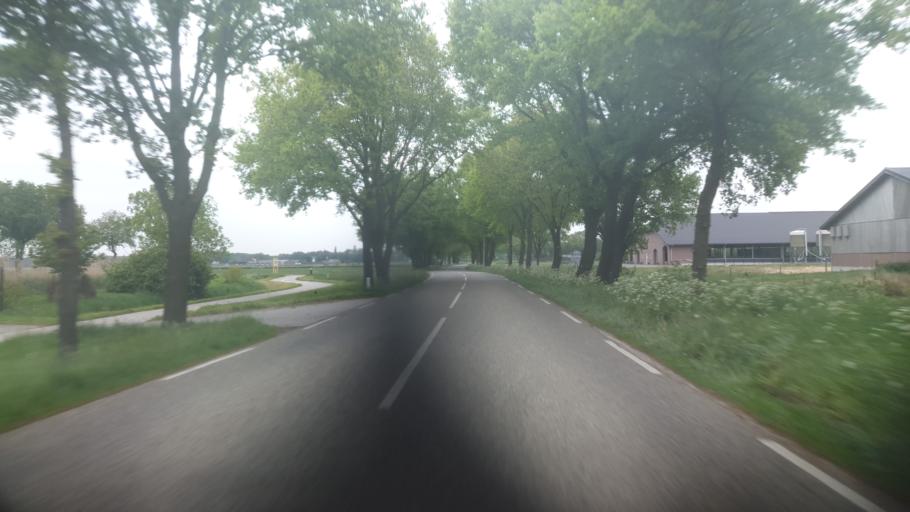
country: NL
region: North Brabant
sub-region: Gemeente Grave
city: Grave
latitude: 51.7722
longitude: 5.7899
